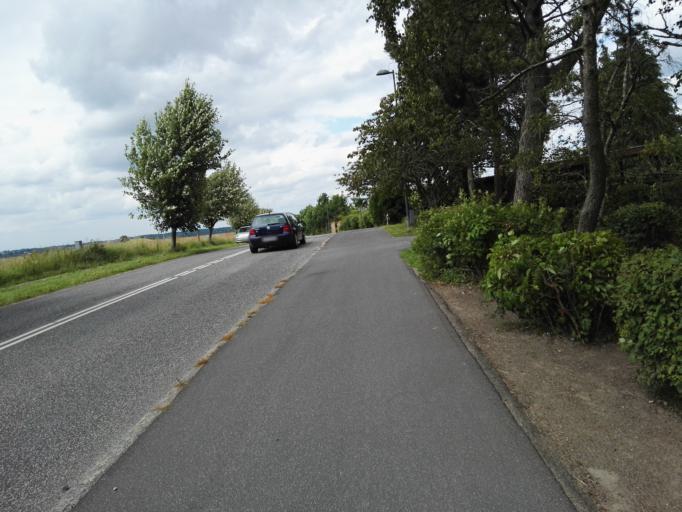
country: DK
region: Capital Region
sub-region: Egedal Kommune
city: Smorumnedre
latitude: 55.7530
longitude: 12.3092
